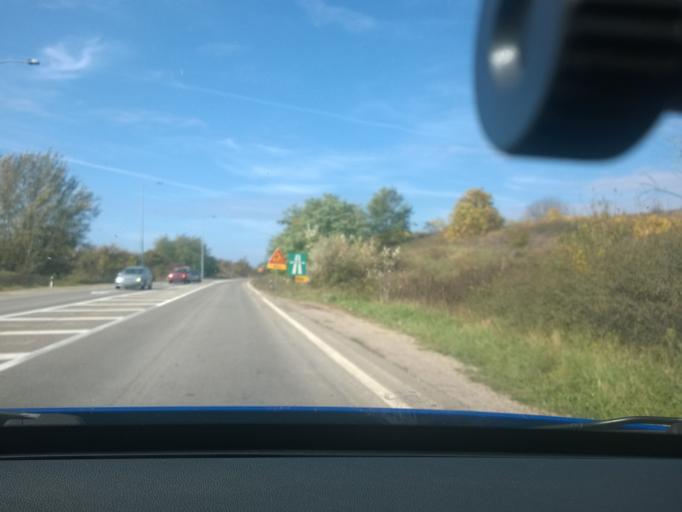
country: RS
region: Central Serbia
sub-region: Nisavski Okrug
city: Niska Banja
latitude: 43.3113
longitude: 22.0373
